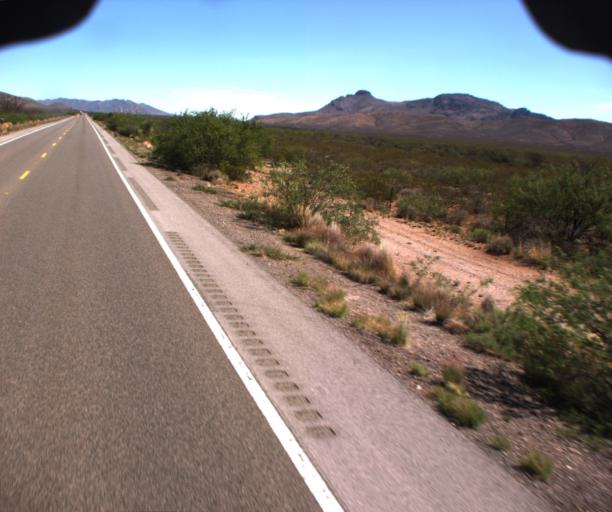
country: US
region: Arizona
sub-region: Cochise County
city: Douglas
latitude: 31.4291
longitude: -109.4846
